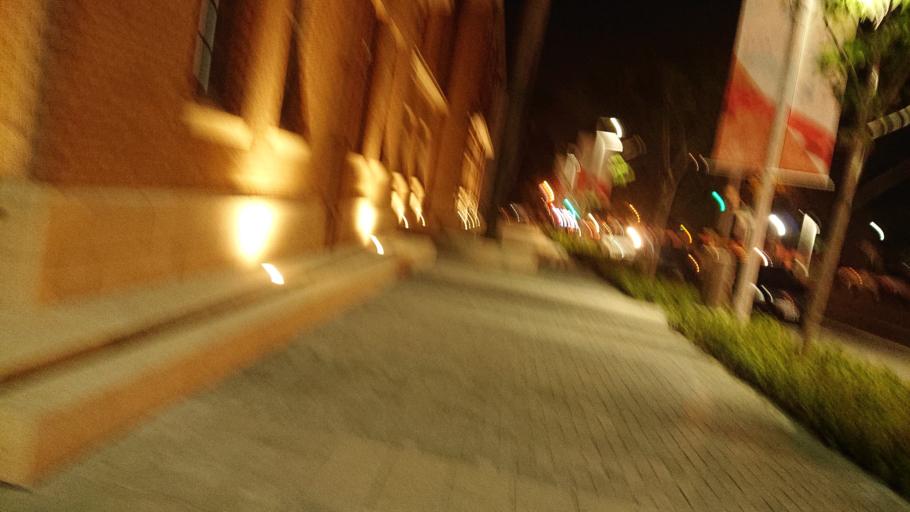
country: TW
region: Taiwan
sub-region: Tainan
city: Tainan
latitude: 22.9914
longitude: 120.2049
